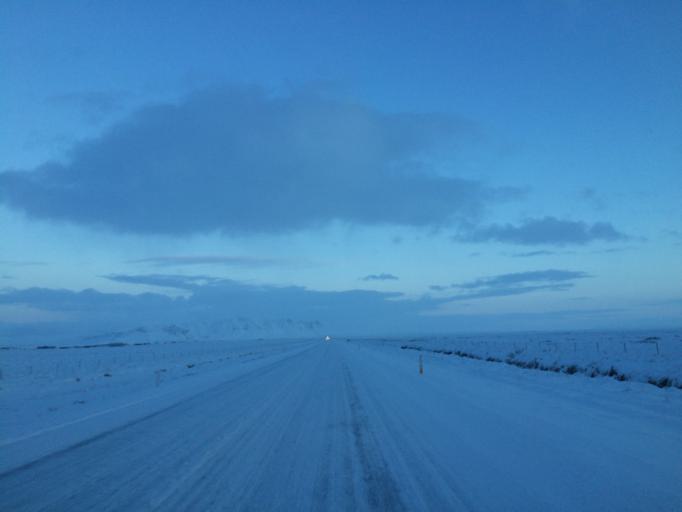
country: IS
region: South
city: Selfoss
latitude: 63.8763
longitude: -21.0925
